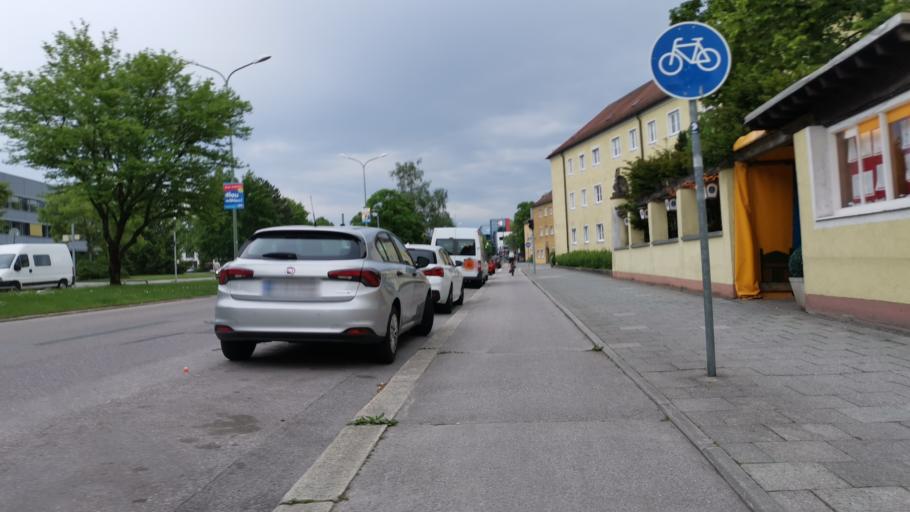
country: DE
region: Bavaria
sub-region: Upper Bavaria
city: Pullach im Isartal
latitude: 48.1014
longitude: 11.5240
